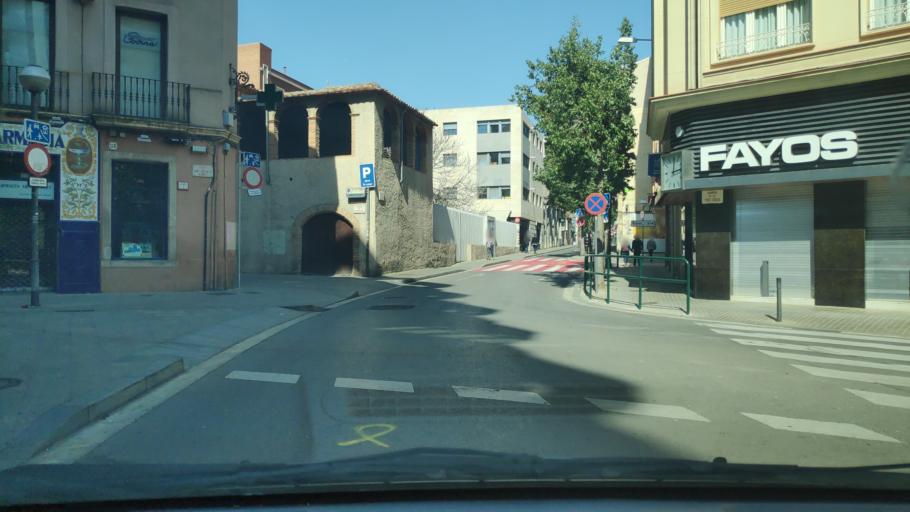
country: ES
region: Catalonia
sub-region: Provincia de Barcelona
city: Sabadell
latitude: 41.5467
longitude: 2.1100
